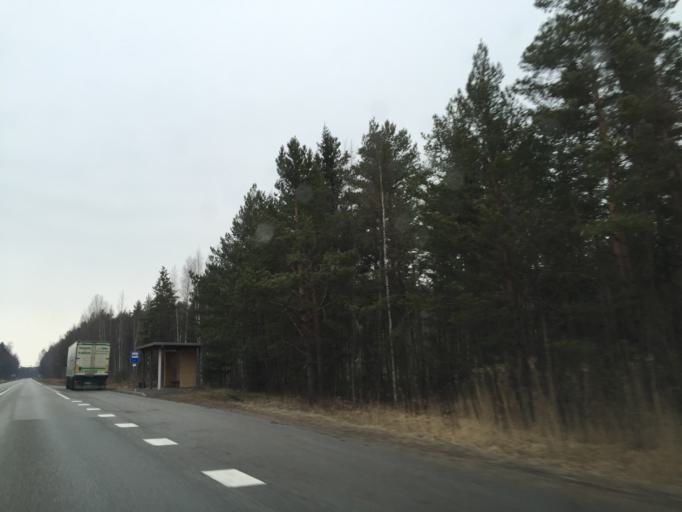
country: LV
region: Salacgrivas
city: Salacgriva
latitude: 57.6153
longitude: 24.3938
